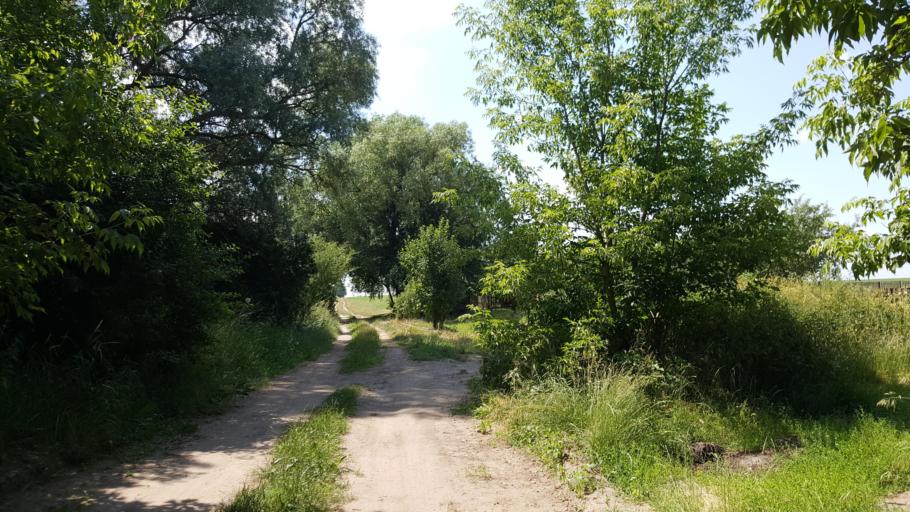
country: BY
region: Brest
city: Kamyanyets
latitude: 52.4052
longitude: 23.7808
